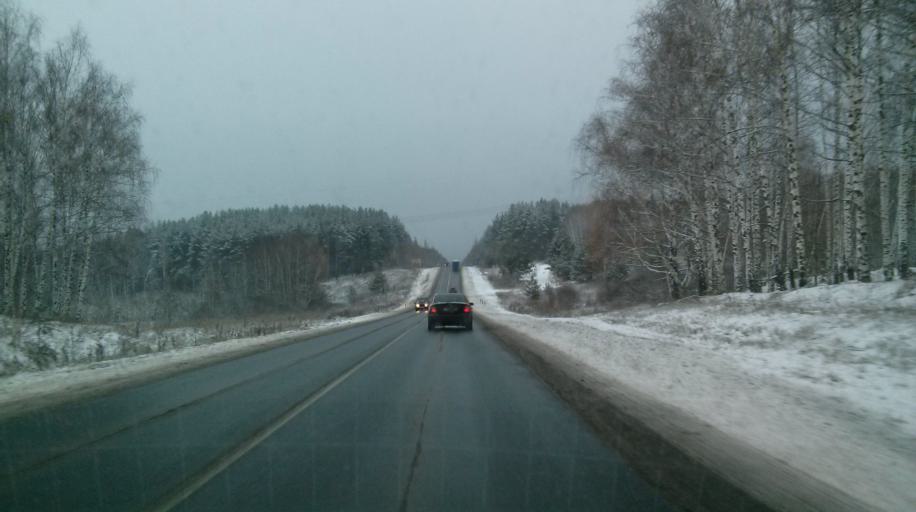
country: RU
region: Nizjnij Novgorod
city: Vorsma
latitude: 56.0263
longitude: 43.3574
